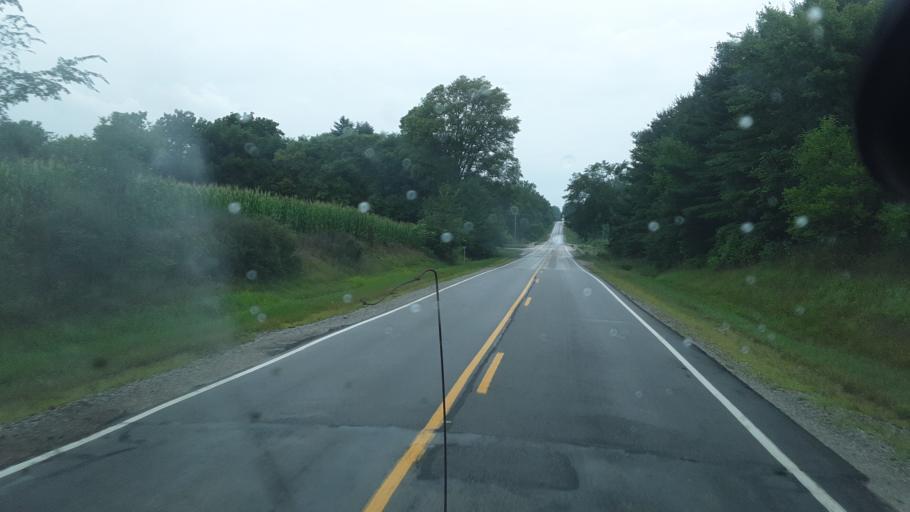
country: US
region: Indiana
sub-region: Steuben County
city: Hamilton
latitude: 41.5590
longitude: -84.8330
